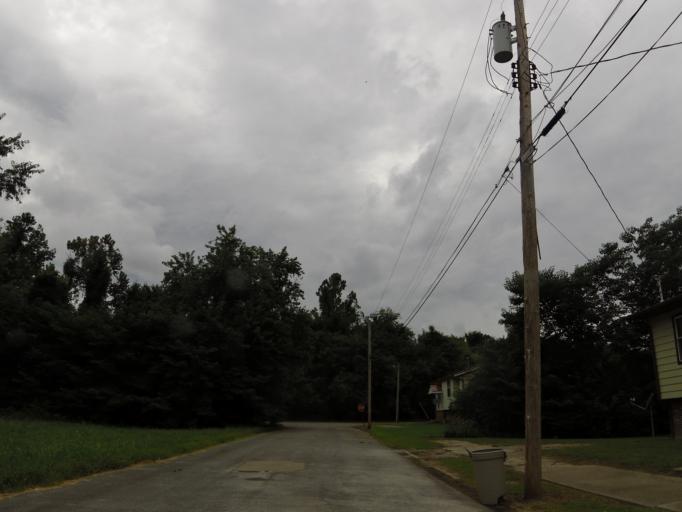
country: US
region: Illinois
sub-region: Alexander County
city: Cairo
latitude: 36.9974
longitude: -89.1687
